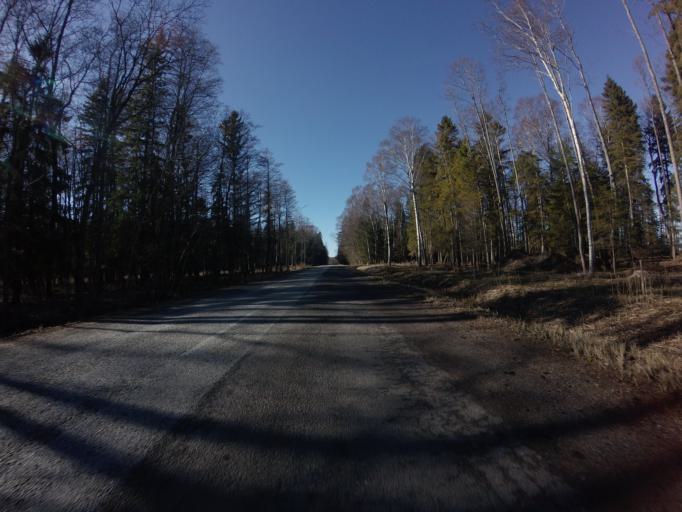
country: EE
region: Saare
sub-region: Kuressaare linn
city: Kuressaare
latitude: 58.5752
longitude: 22.6433
